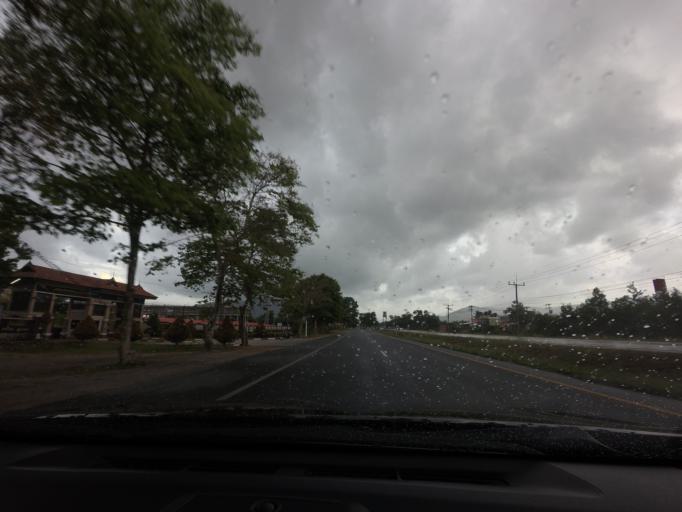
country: TH
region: Pattani
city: Mayo
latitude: 6.7663
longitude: 101.4692
